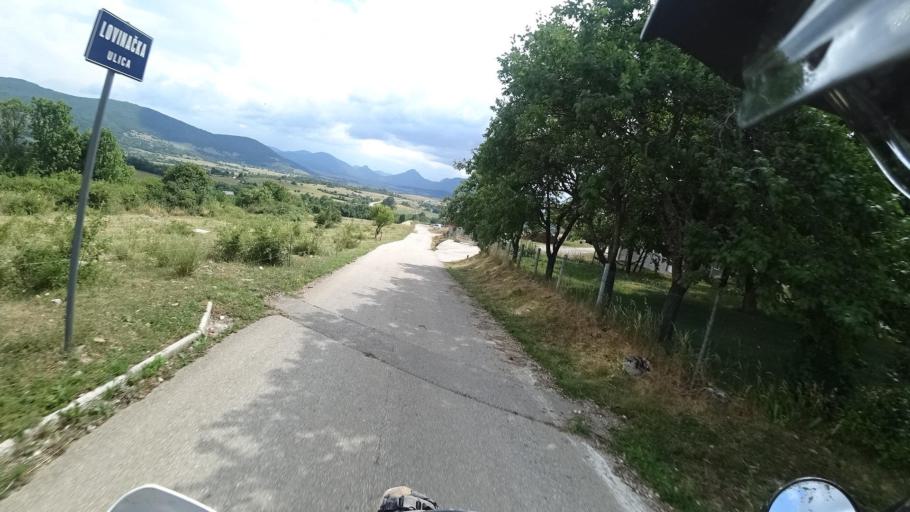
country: HR
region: Zadarska
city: Gracac
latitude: 44.5281
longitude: 15.7660
